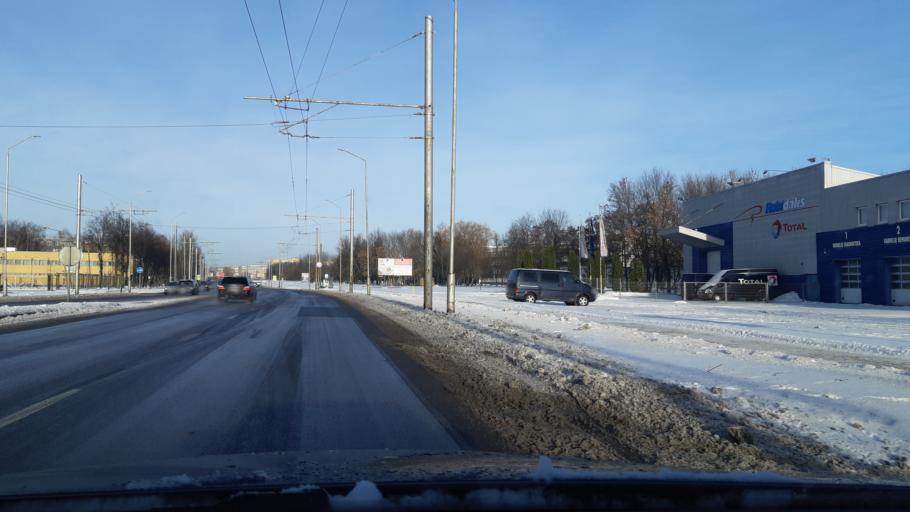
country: LT
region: Kauno apskritis
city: Dainava (Kaunas)
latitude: 54.9182
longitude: 23.9843
